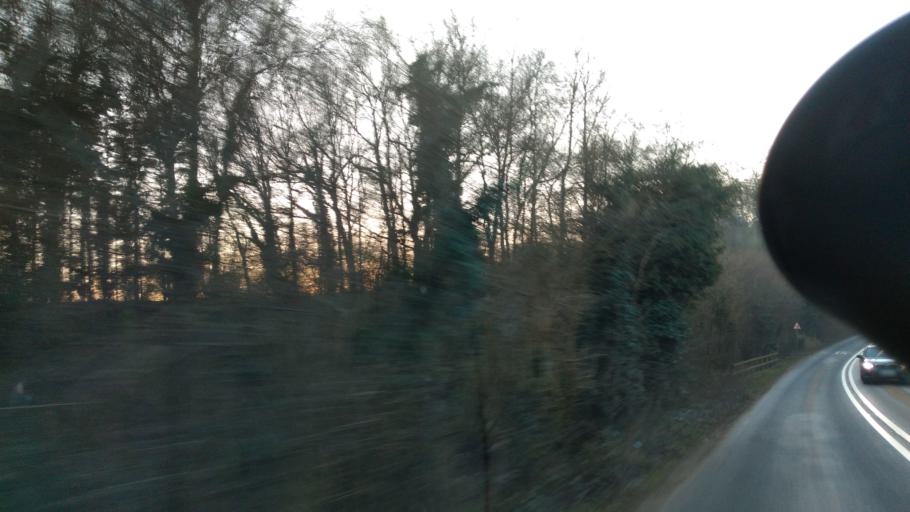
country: GB
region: England
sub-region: Wiltshire
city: Calne
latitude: 51.4097
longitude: -2.0274
